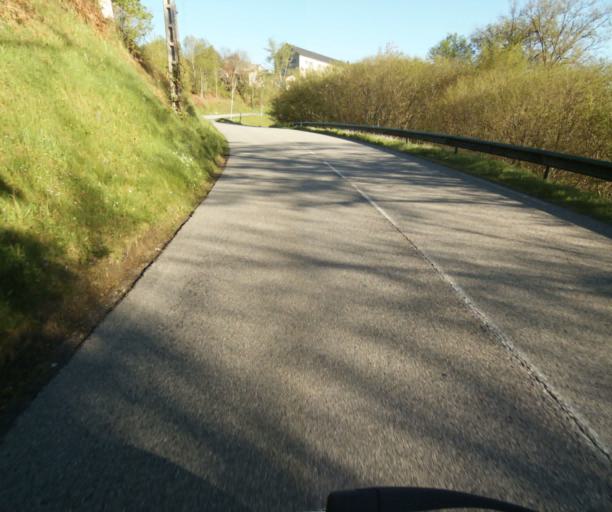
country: FR
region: Limousin
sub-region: Departement de la Correze
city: Correze
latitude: 45.3661
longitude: 1.8737
